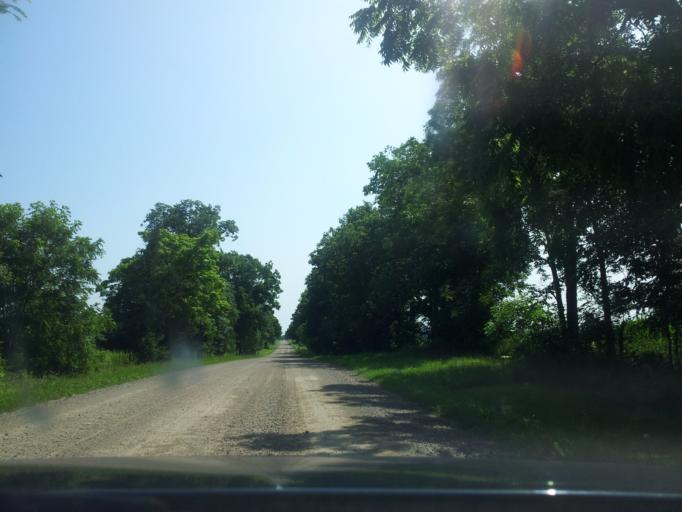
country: CA
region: Ontario
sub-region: Oxford County
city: Woodstock
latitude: 42.9539
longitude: -80.6208
